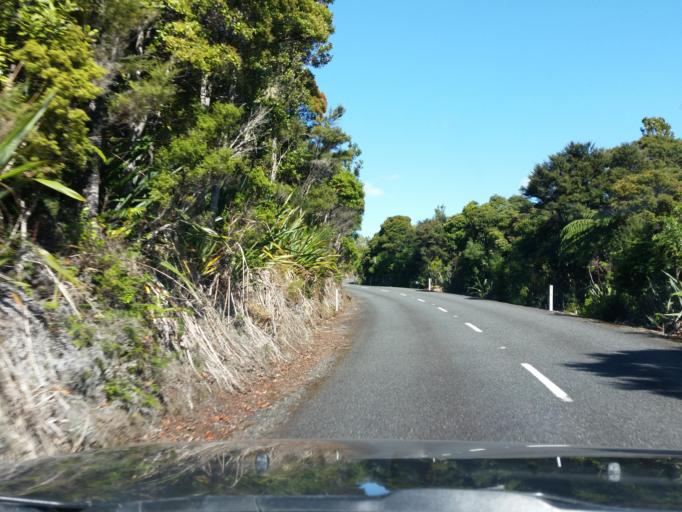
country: NZ
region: Northland
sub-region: Kaipara District
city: Dargaville
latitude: -35.6785
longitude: 173.5741
